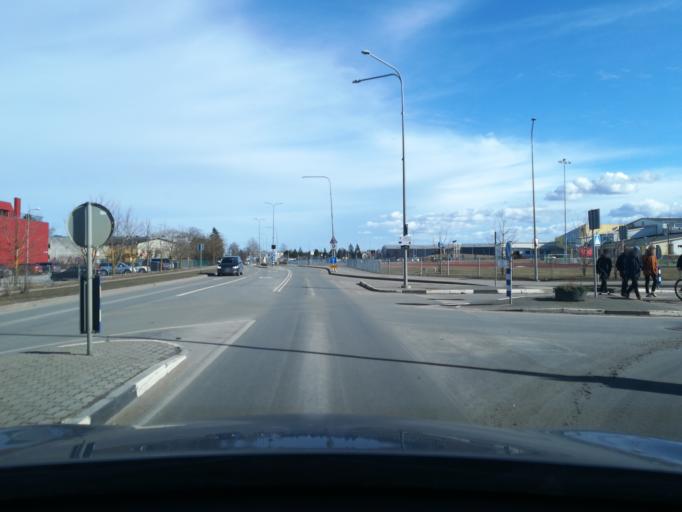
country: EE
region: Harju
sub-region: Saue vald
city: Laagri
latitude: 59.3514
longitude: 24.6153
